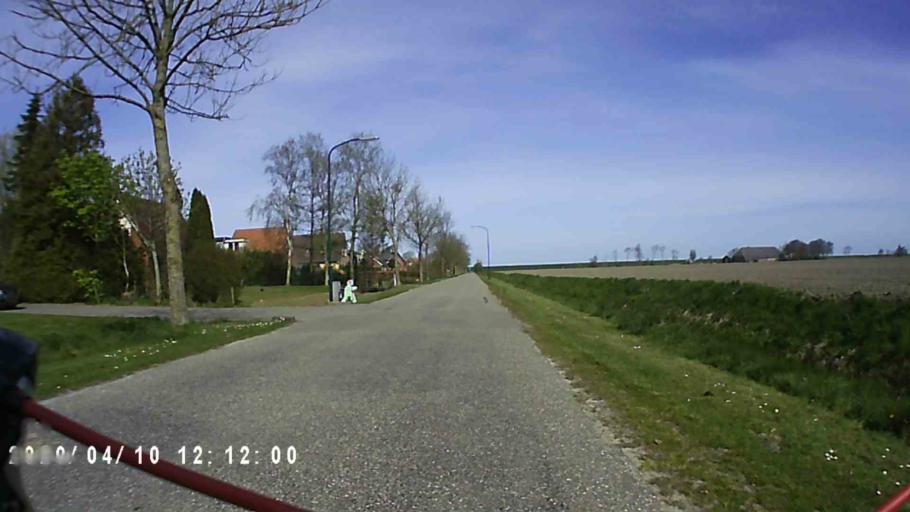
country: NL
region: Groningen
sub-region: Gemeente De Marne
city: Ulrum
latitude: 53.3909
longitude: 6.3742
